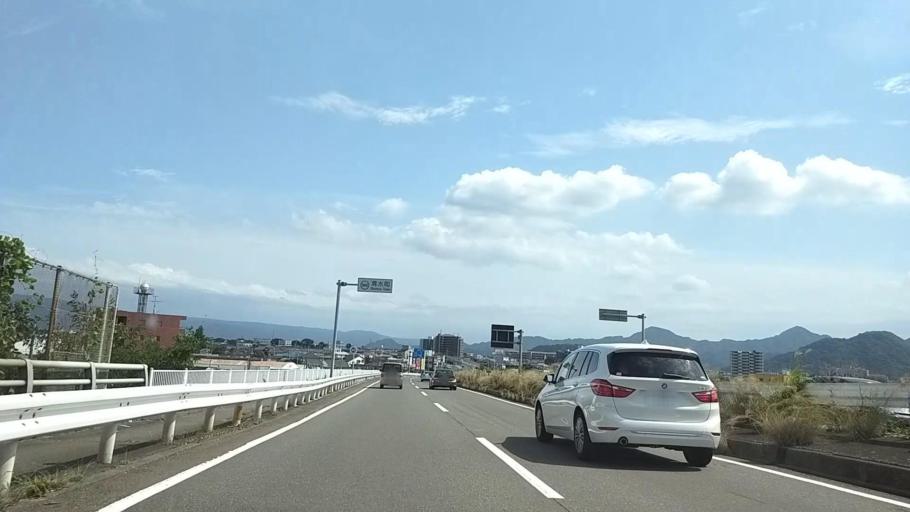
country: JP
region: Shizuoka
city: Mishima
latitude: 35.1162
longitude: 138.8896
